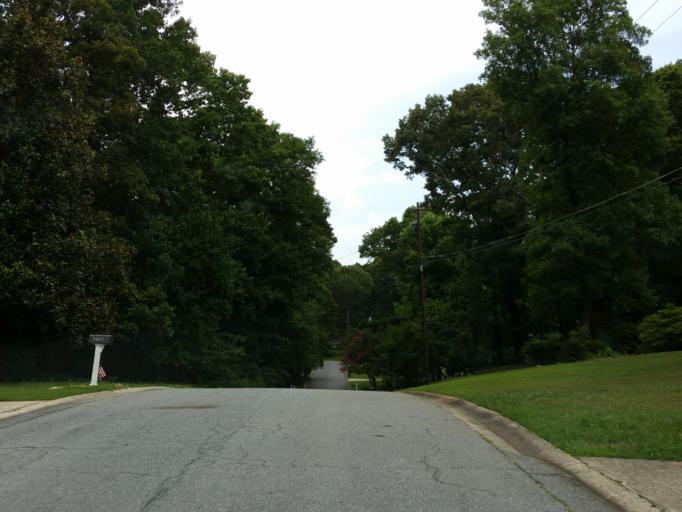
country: US
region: Georgia
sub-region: Cherokee County
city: Woodstock
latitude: 34.0199
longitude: -84.4749
